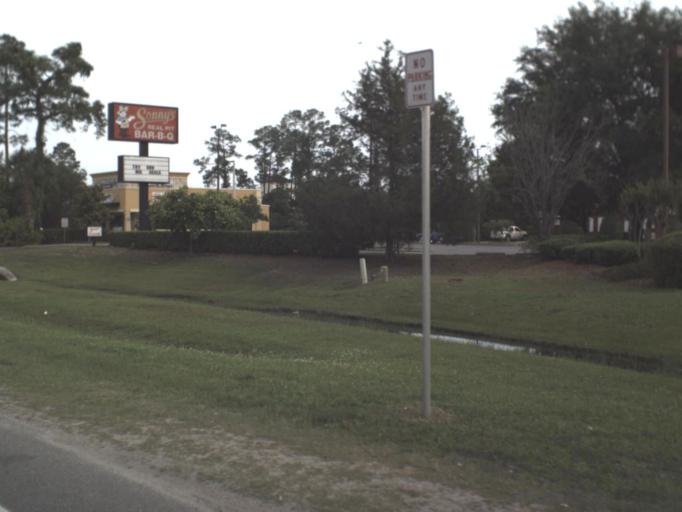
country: US
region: Florida
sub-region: Saint Johns County
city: Saint Augustine
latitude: 29.9210
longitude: -81.4165
